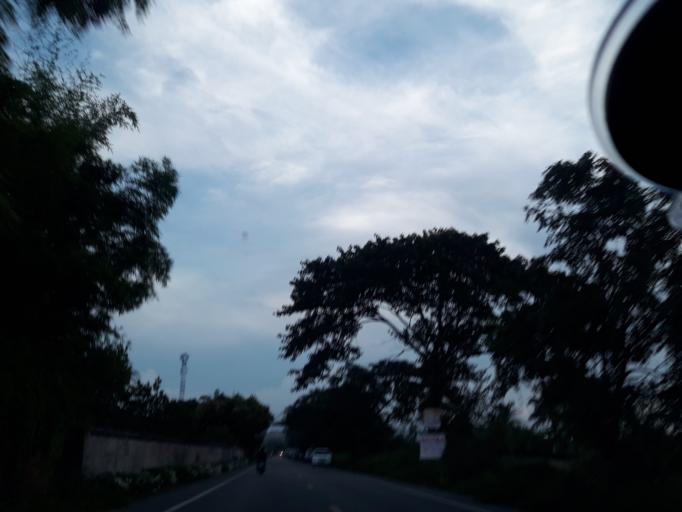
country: TH
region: Pathum Thani
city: Nong Suea
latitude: 14.1384
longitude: 100.8690
